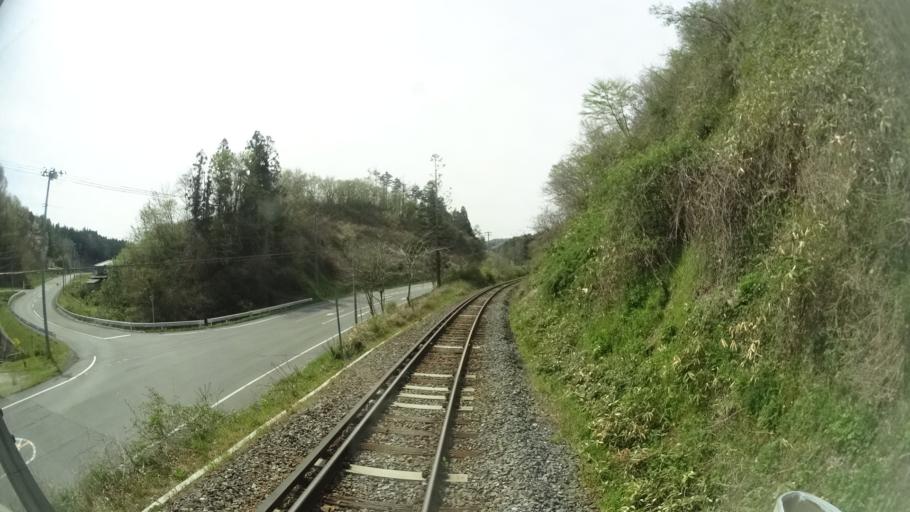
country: JP
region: Iwate
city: Ichinoseki
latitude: 38.9775
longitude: 141.3306
